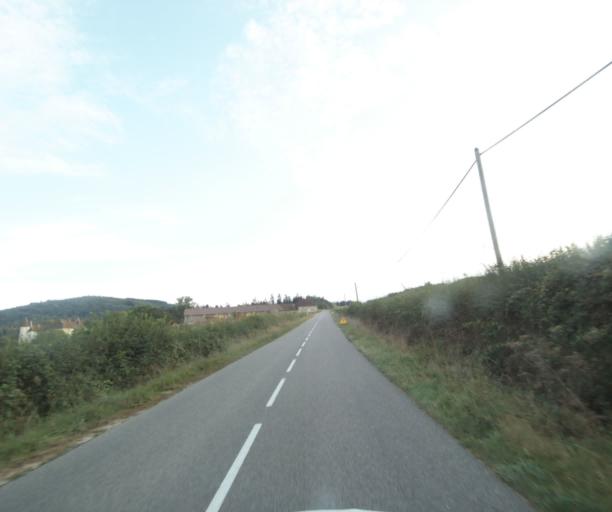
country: FR
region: Bourgogne
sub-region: Departement de Saone-et-Loire
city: Charolles
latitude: 46.4244
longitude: 4.4047
